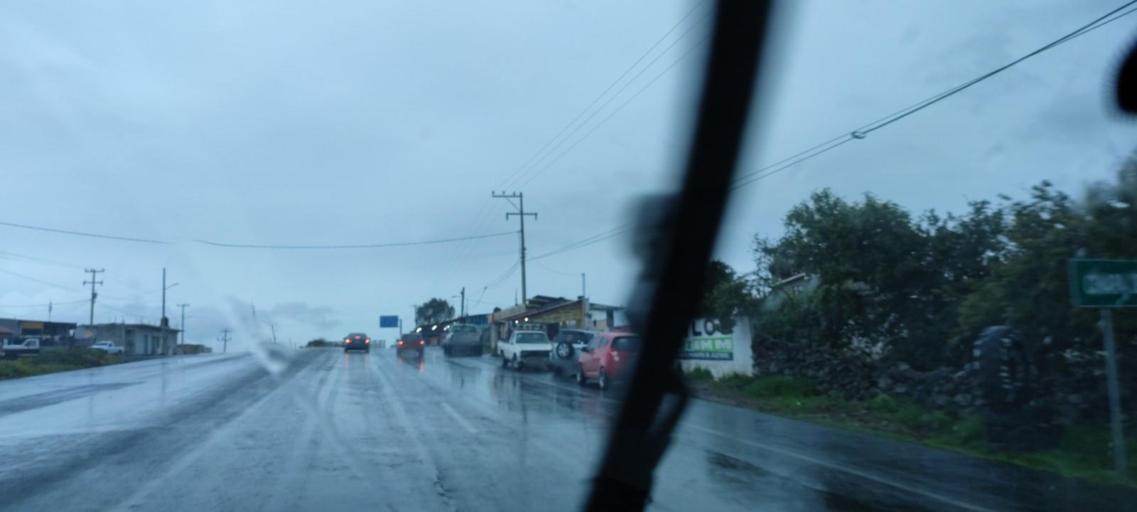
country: MX
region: Mexico
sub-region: Jilotepec
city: Doxhicho
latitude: 19.9249
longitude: -99.5844
